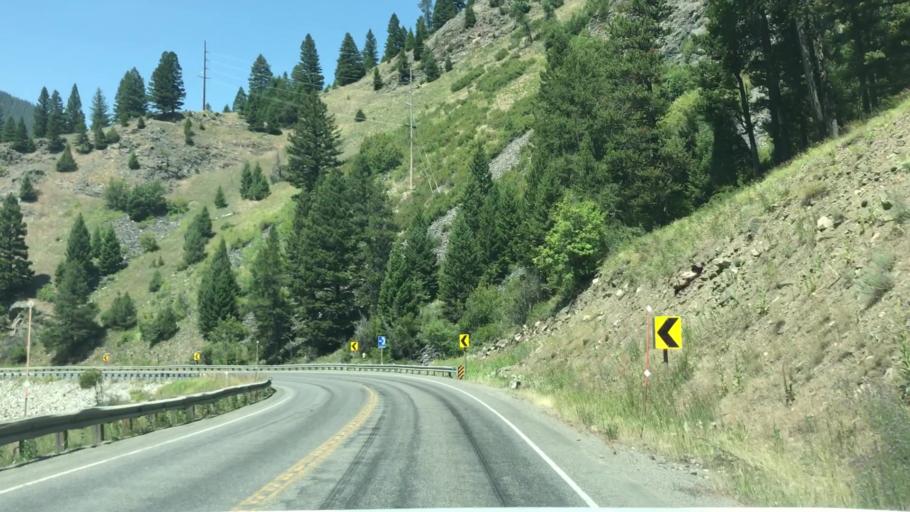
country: US
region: Montana
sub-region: Gallatin County
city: Big Sky
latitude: 45.4068
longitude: -111.2210
